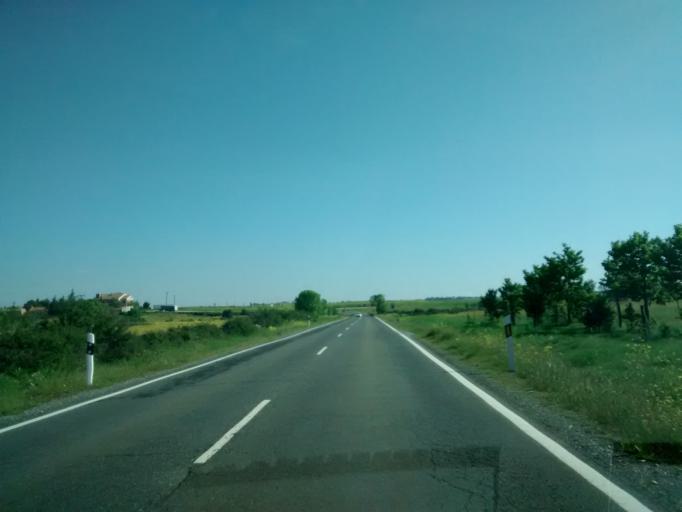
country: ES
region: Castille and Leon
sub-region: Provincia de Segovia
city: Trescasas
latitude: 40.9595
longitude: -4.0333
